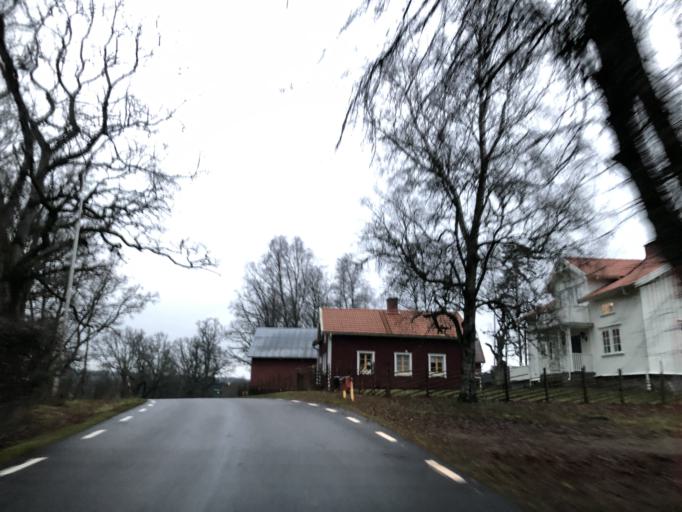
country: SE
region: Vaestra Goetaland
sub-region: Boras Kommun
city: Dalsjofors
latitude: 57.8353
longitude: 13.2181
